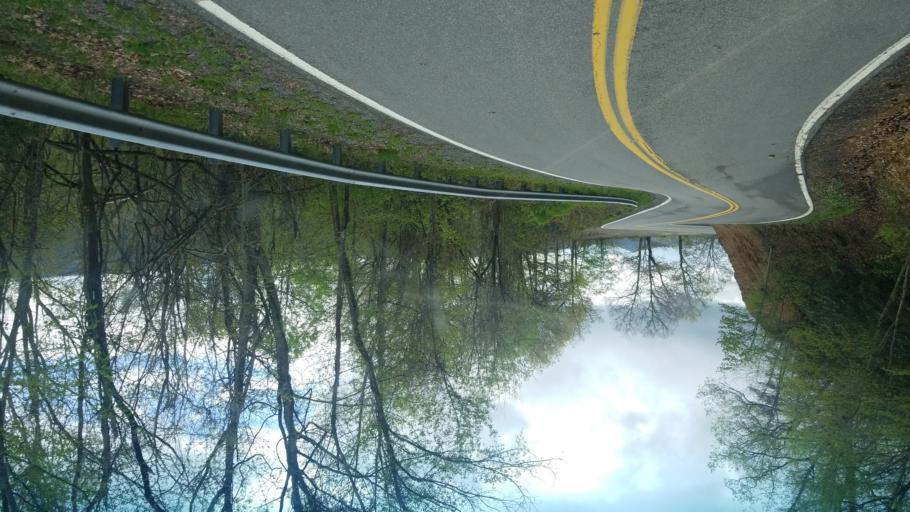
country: US
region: Virginia
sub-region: Tazewell County
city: Tazewell
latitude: 37.0066
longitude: -81.5186
